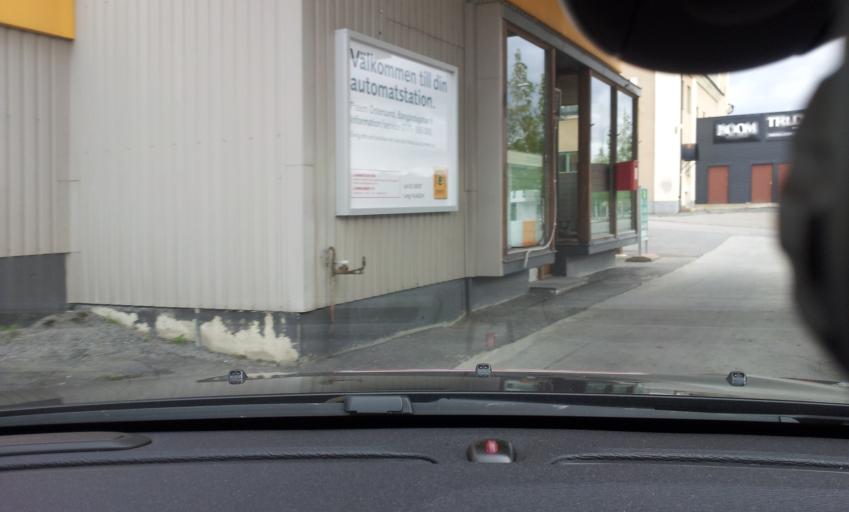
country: SE
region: Jaemtland
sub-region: OEstersunds Kommun
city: Ostersund
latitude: 63.1692
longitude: 14.6420
